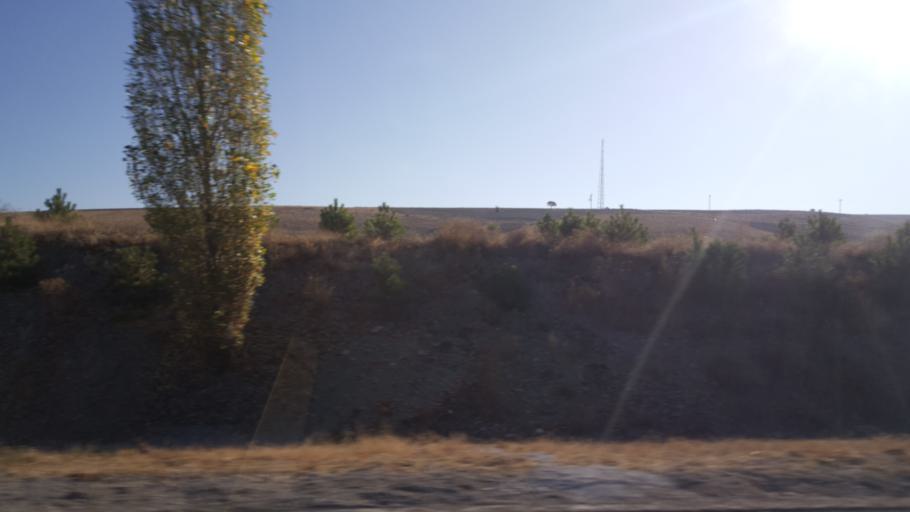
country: TR
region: Ankara
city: Cankaya
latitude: 39.8468
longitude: 32.8926
